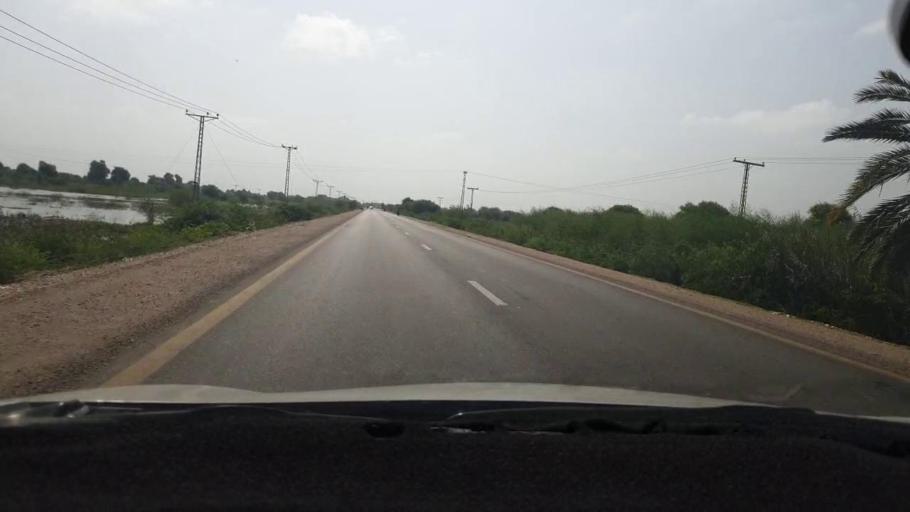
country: PK
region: Sindh
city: Mirpur Khas
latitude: 25.7344
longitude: 69.1019
